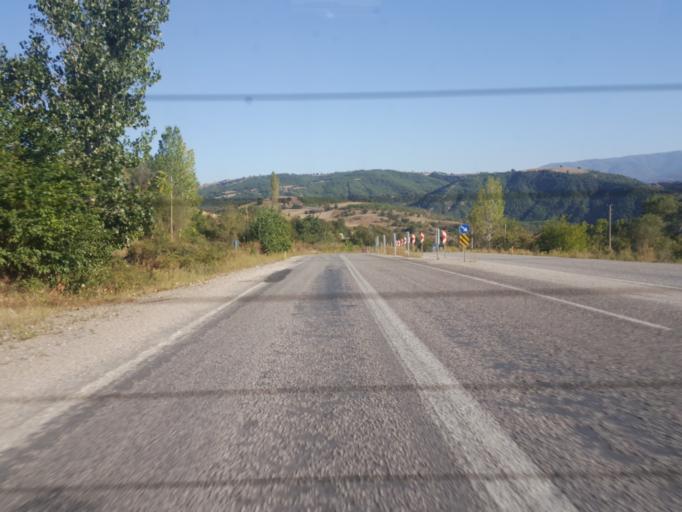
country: TR
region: Amasya
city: Tasova
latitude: 40.7636
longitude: 36.2809
